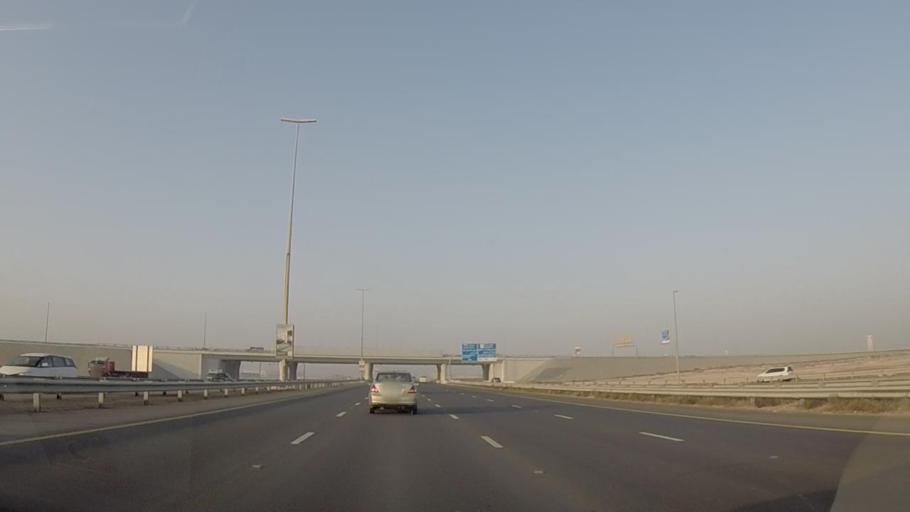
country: AE
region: Dubai
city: Dubai
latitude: 24.9477
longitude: 55.0641
